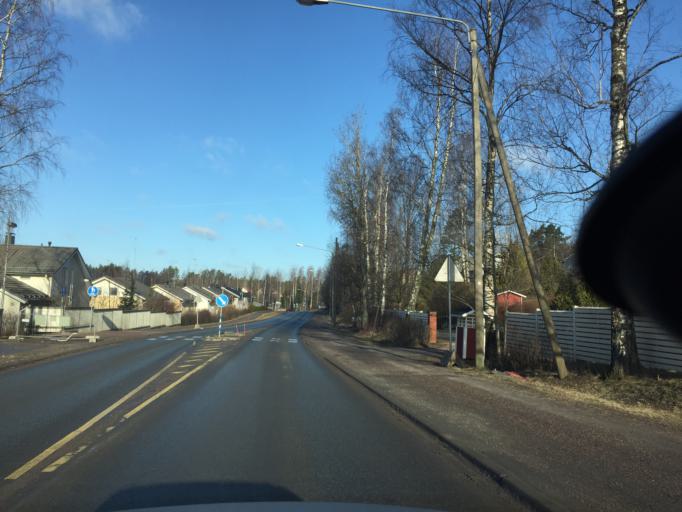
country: FI
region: Uusimaa
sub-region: Helsinki
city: Helsinki
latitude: 60.2823
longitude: 24.9220
